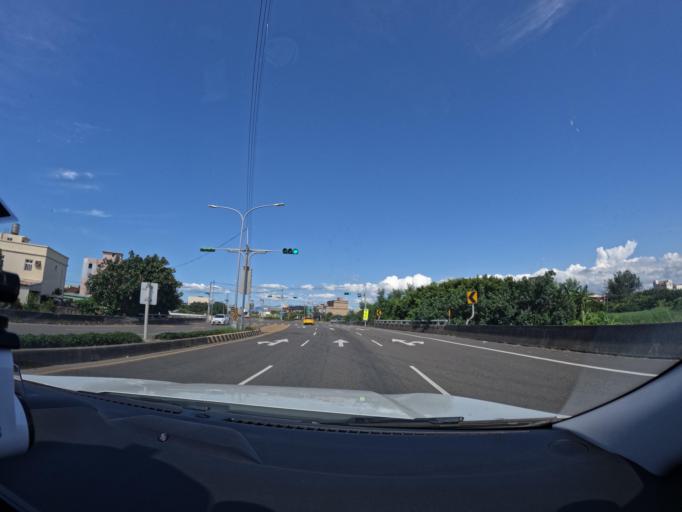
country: TW
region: Taiwan
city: Taoyuan City
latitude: 25.1067
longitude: 121.2394
